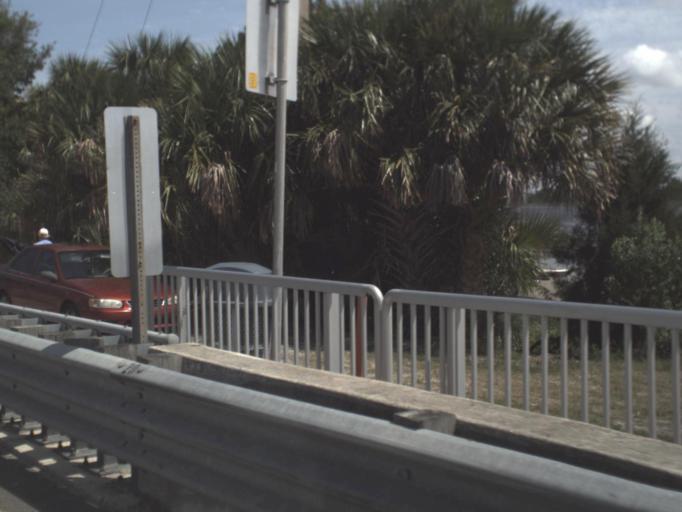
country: US
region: Florida
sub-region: Duval County
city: Jacksonville
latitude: 30.4172
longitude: -81.5300
